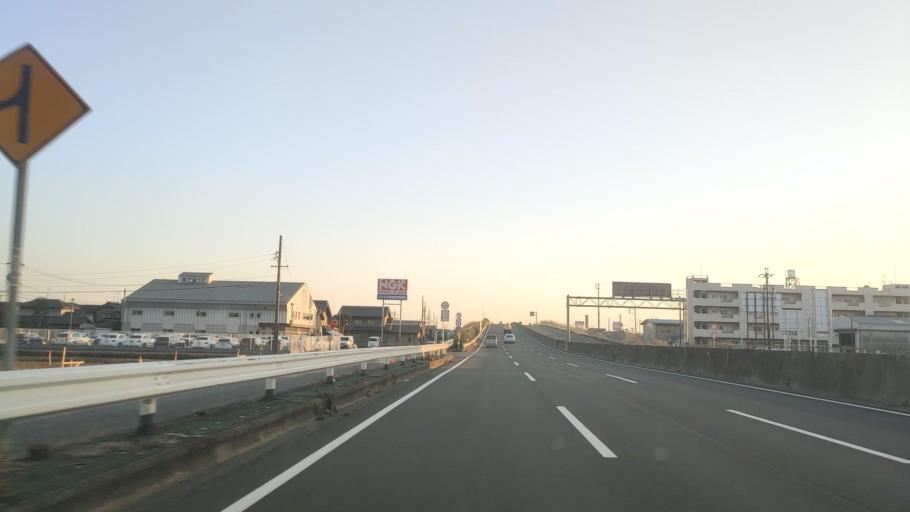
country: JP
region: Gifu
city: Kasamatsucho
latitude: 35.3783
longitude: 136.7844
